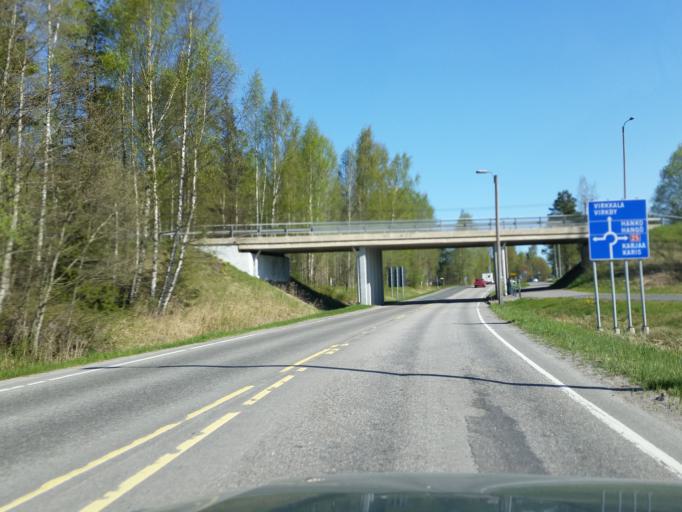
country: FI
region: Uusimaa
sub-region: Helsinki
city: Lohja
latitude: 60.1780
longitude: 23.9902
